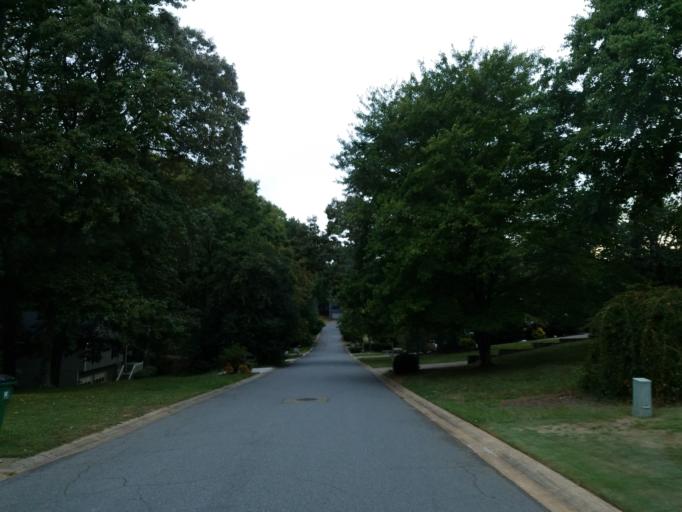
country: US
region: Georgia
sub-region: Fulton County
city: Sandy Springs
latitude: 33.9739
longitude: -84.4176
